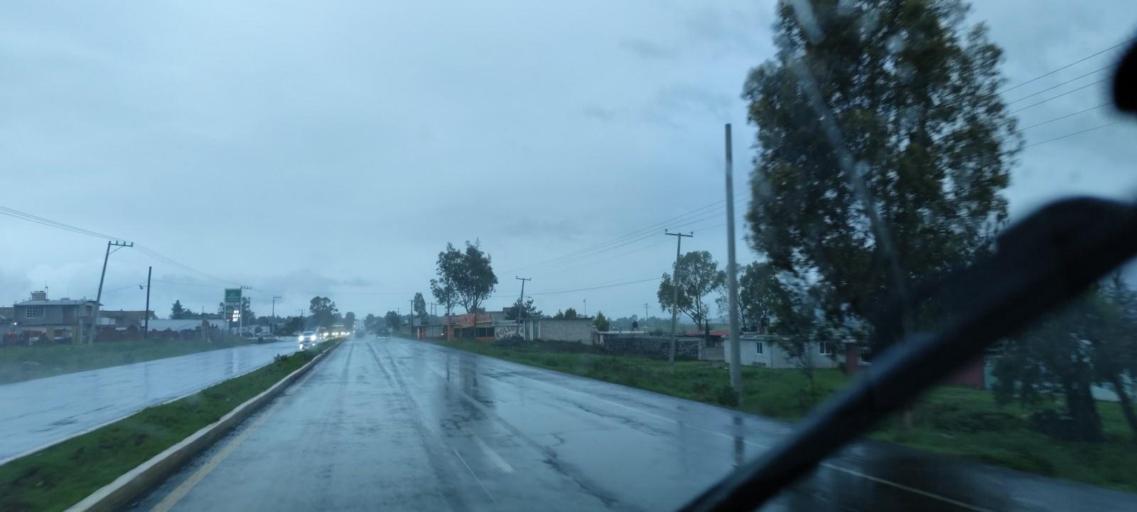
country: MX
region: Mexico
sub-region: Jilotepec
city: Doxhicho
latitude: 19.9164
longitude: -99.5990
